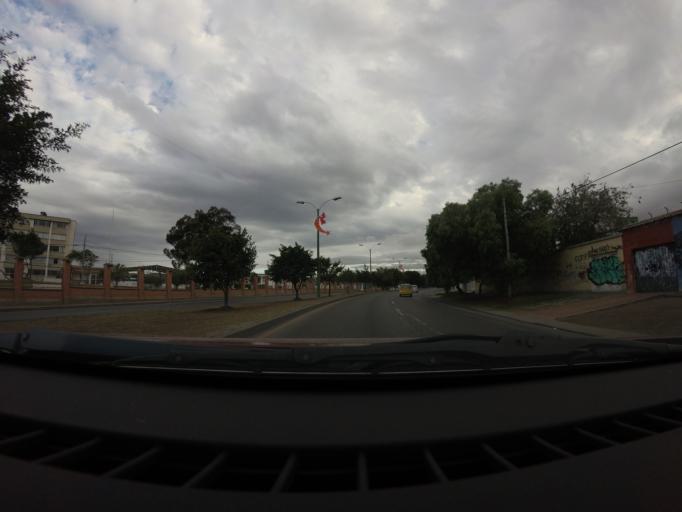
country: CO
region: Boyaca
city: Tunja
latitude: 5.5417
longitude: -73.3564
